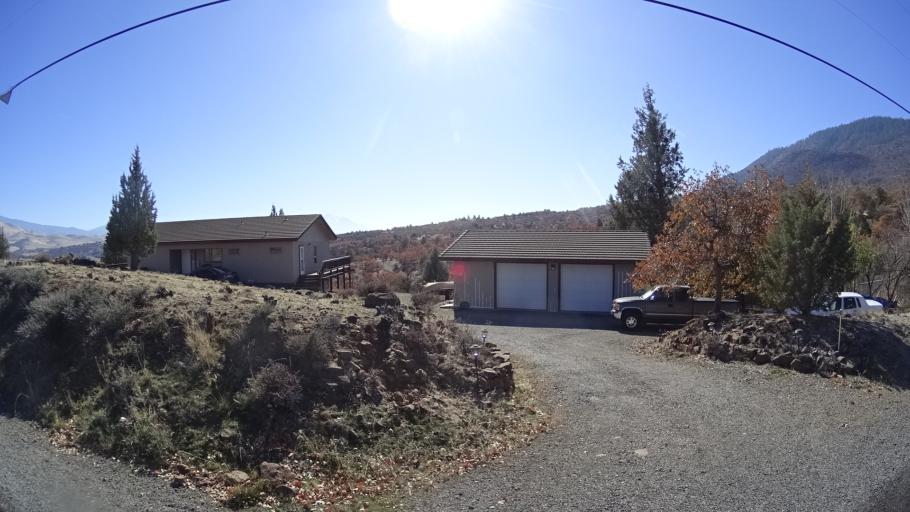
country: US
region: California
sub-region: Siskiyou County
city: Montague
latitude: 41.8760
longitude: -122.4848
